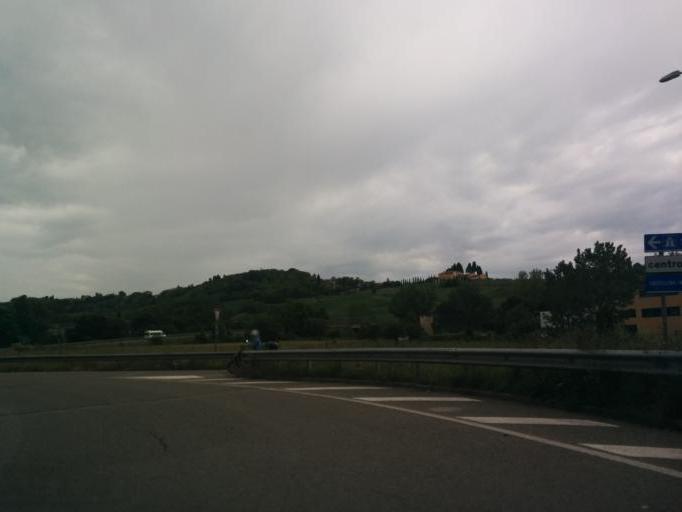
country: IT
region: Tuscany
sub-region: Provincia di Siena
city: Poggibonsi
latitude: 43.4861
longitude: 11.1503
